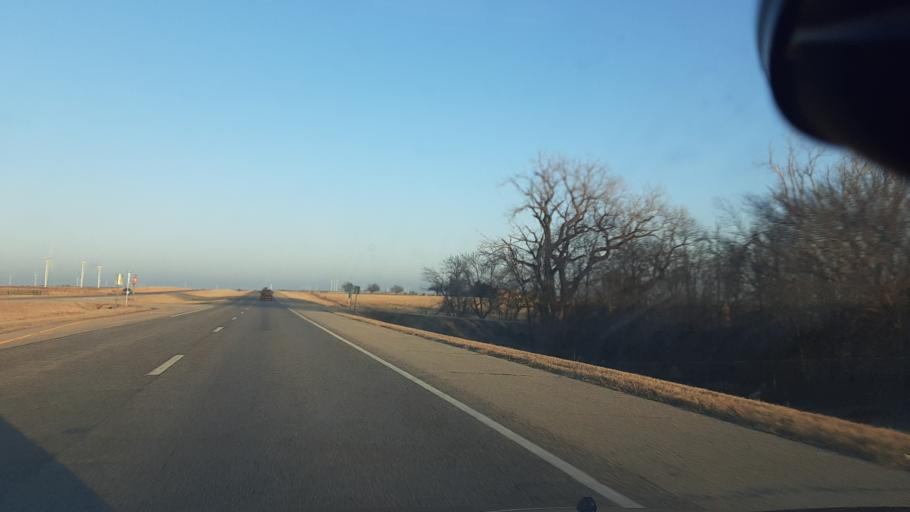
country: US
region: Oklahoma
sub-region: Noble County
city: Perry
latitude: 36.3978
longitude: -97.5156
